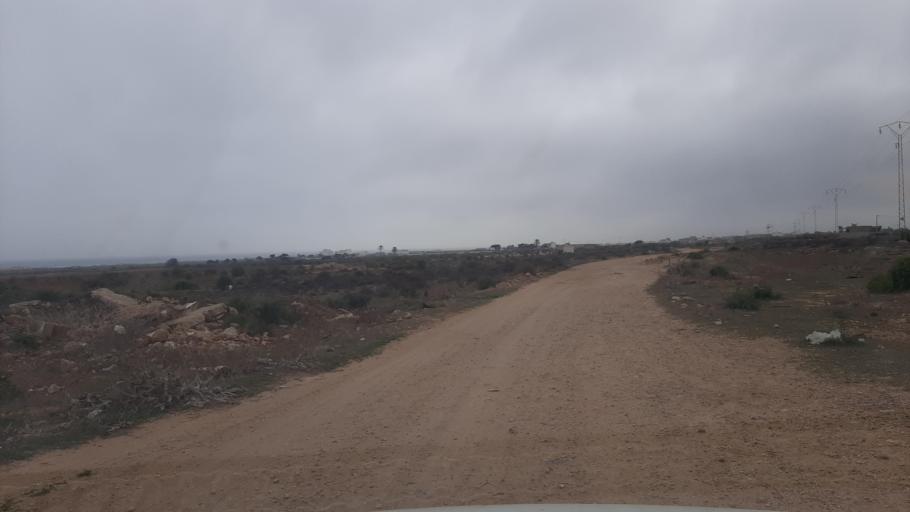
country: TN
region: Nabul
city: Menzel Heurr
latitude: 36.6934
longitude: 10.9358
